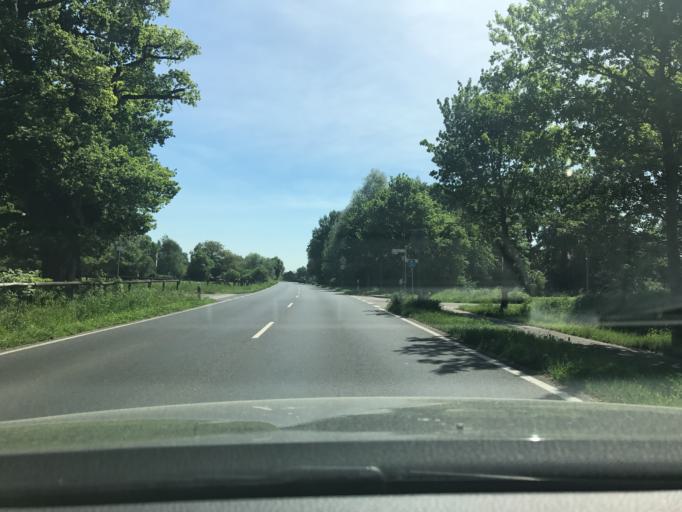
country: DE
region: North Rhine-Westphalia
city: Kempen
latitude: 51.3727
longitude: 6.4662
